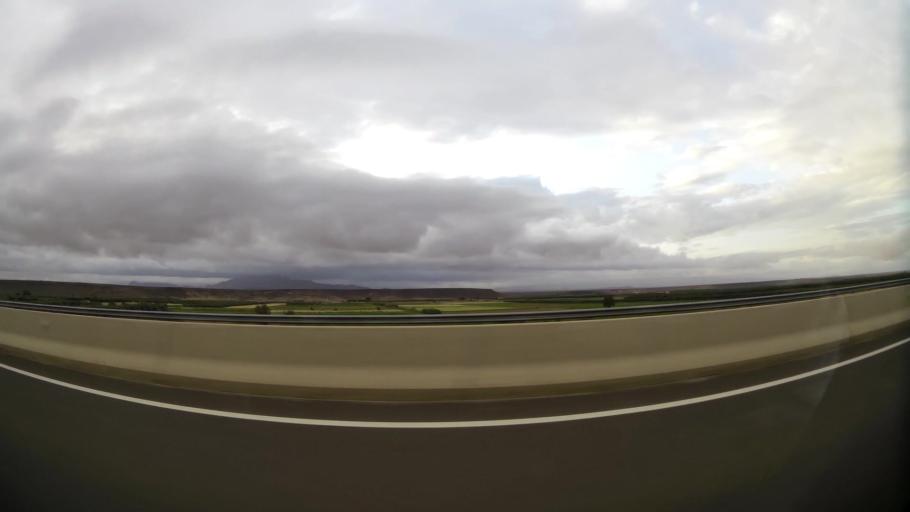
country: MA
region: Taza-Al Hoceima-Taounate
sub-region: Taza
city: Guercif
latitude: 34.3994
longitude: -3.1992
